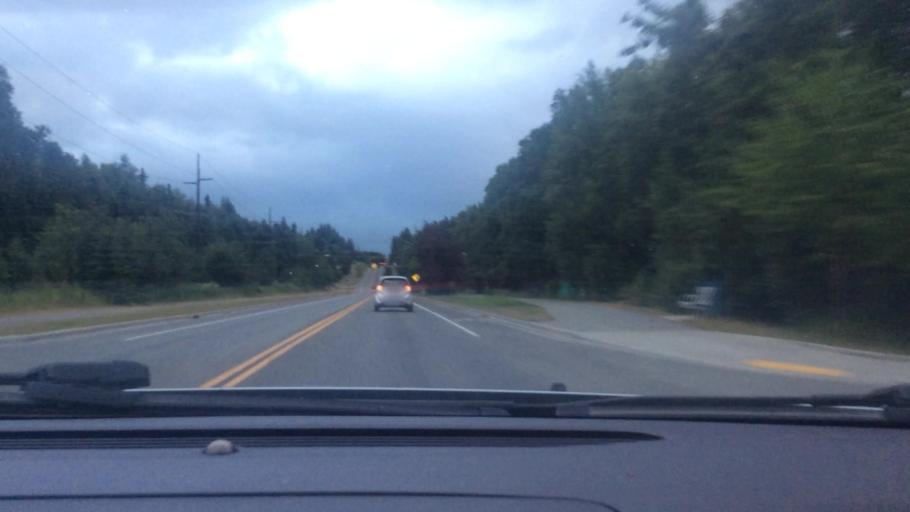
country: US
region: Alaska
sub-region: Anchorage Municipality
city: Anchorage
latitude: 61.1470
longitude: -149.8043
